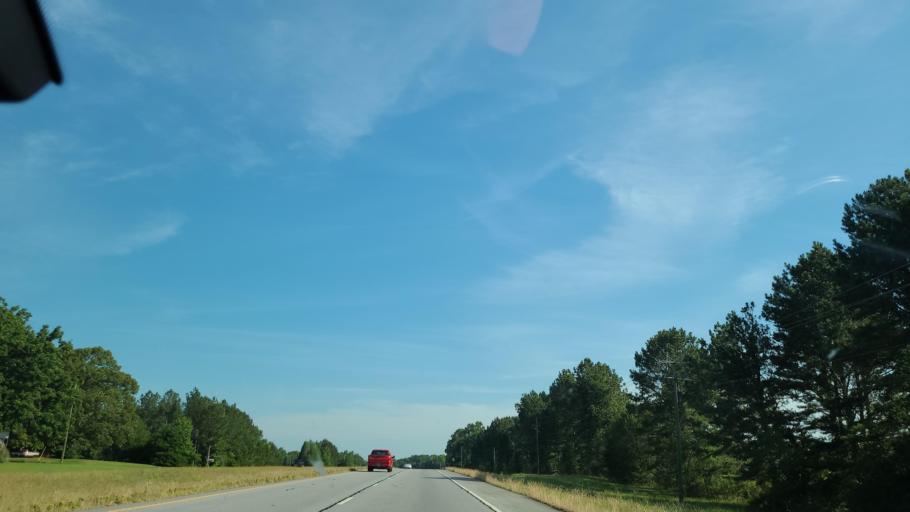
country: US
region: Georgia
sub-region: Clarke County
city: Country Club Estates
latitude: 34.0439
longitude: -83.4041
